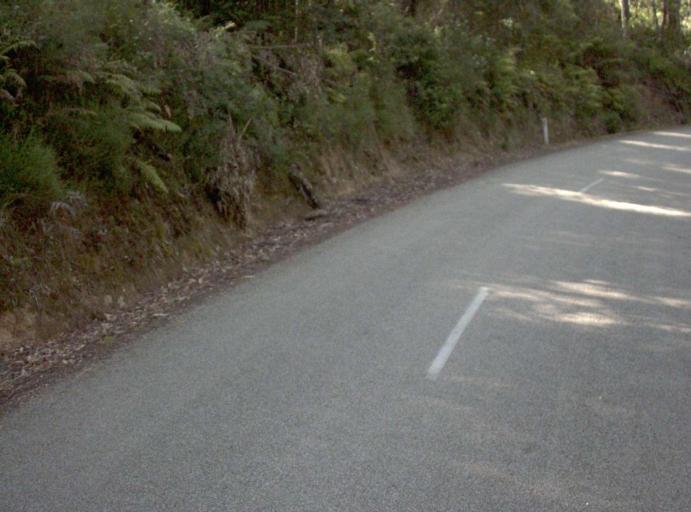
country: AU
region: Victoria
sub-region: East Gippsland
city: Lakes Entrance
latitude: -37.4311
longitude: 148.5985
